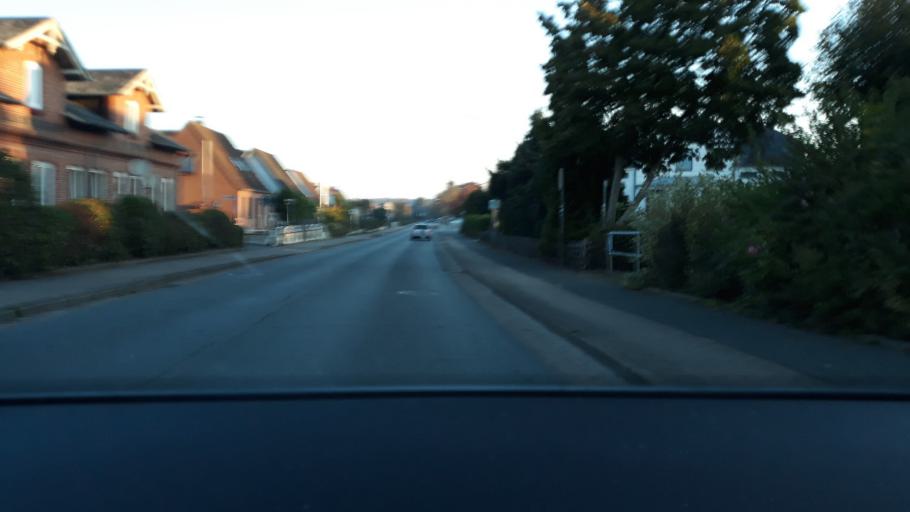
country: DE
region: Schleswig-Holstein
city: Satrup
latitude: 54.6929
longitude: 9.6039
